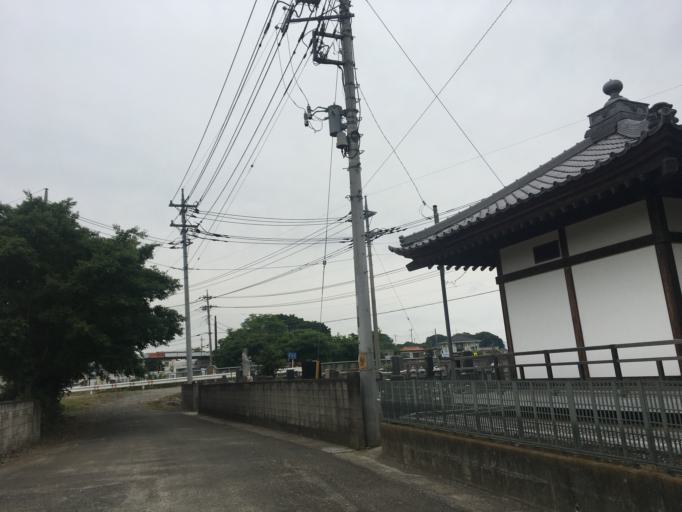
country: JP
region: Saitama
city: Sakado
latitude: 36.0032
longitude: 139.4380
